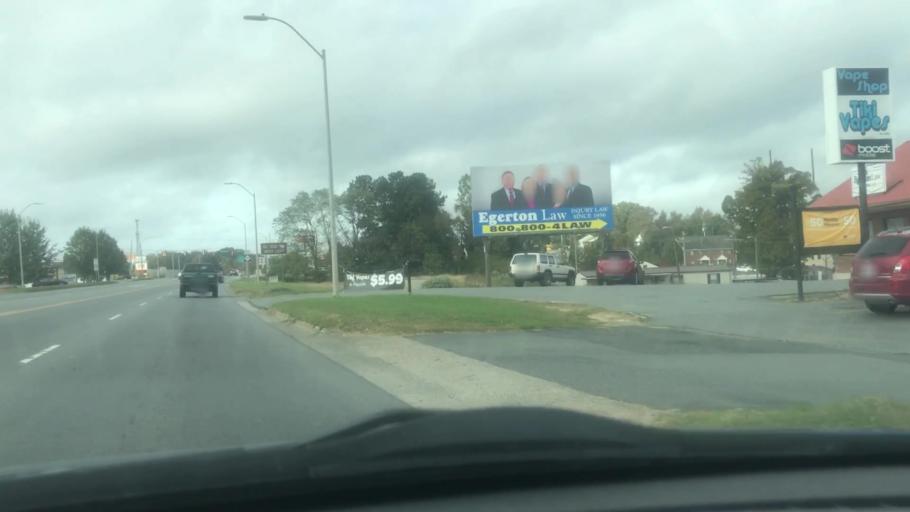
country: US
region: North Carolina
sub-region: Randolph County
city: Asheboro
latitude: 35.6894
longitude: -79.8077
